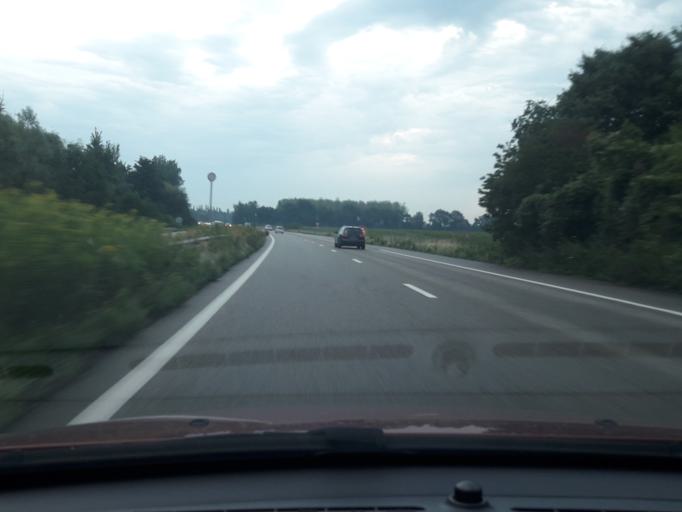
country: FR
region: Alsace
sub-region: Departement du Bas-Rhin
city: La Wantzenau
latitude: 48.6828
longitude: 7.8125
